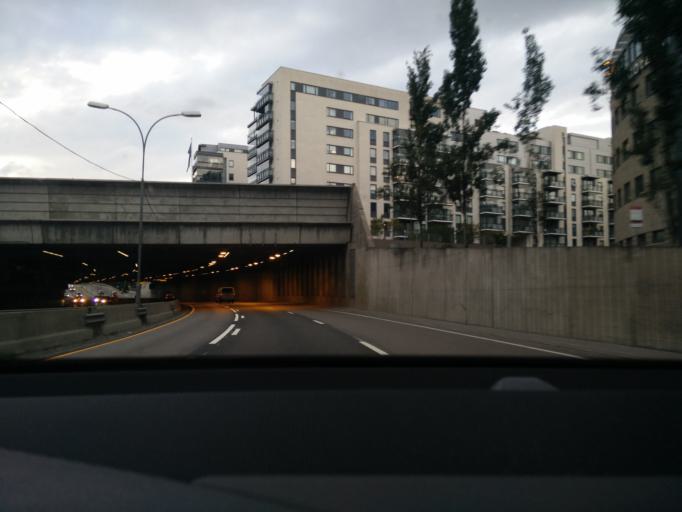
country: NO
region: Oslo
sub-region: Oslo
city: Sjolyststranda
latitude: 59.9196
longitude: 10.6818
